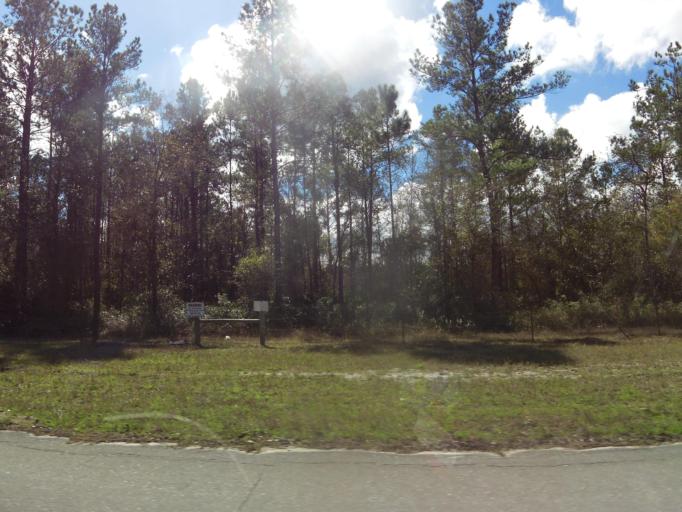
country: US
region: Florida
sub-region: Clay County
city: Green Cove Springs
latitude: 29.8680
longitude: -81.7046
